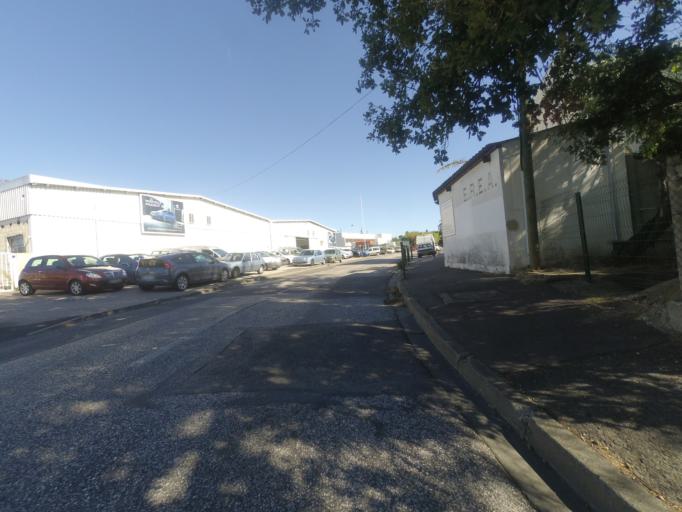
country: FR
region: Languedoc-Roussillon
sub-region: Departement des Pyrenees-Orientales
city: Perpignan
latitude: 42.6790
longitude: 2.8942
